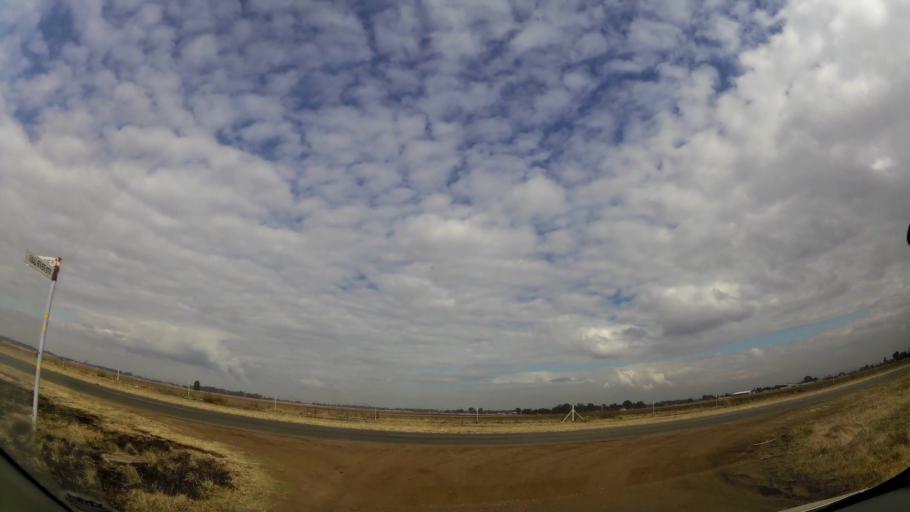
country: ZA
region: Gauteng
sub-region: Sedibeng District Municipality
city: Meyerton
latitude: -26.6109
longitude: 28.0482
